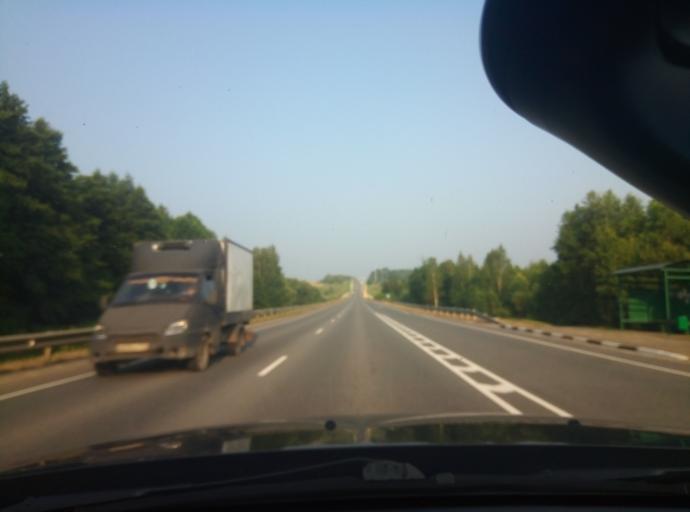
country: RU
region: Tula
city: Novogurovskiy
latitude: 54.2807
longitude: 37.1857
